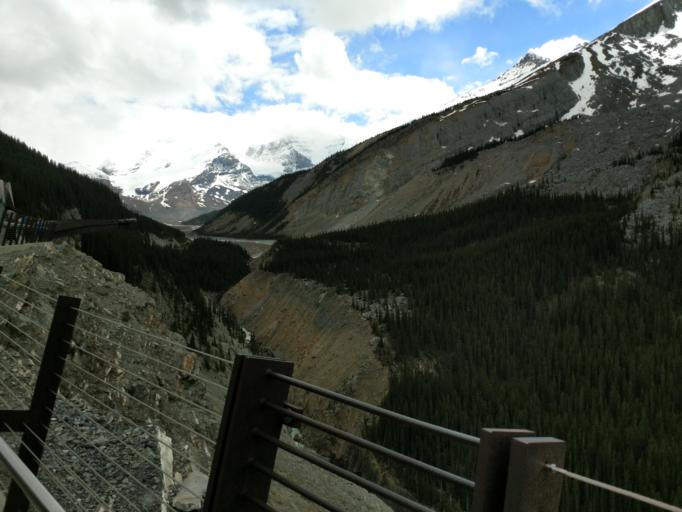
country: CA
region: Alberta
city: Jasper Park Lodge
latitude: 52.2604
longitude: -117.2794
